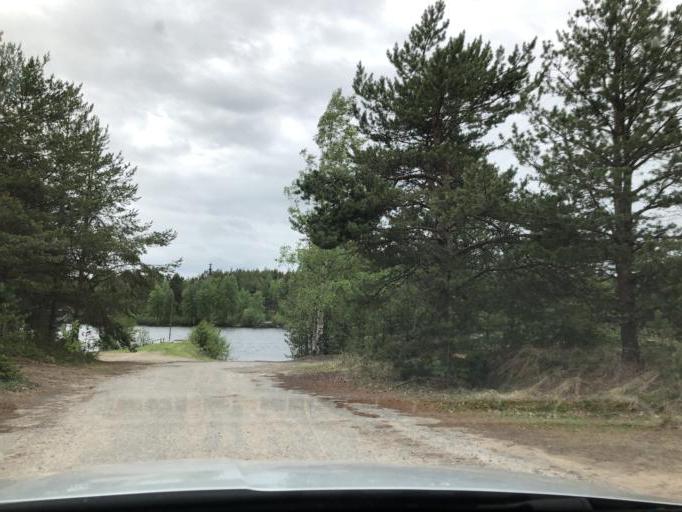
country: SE
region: Norrbotten
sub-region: Pitea Kommun
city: Pitea
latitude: 65.2354
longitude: 21.5145
